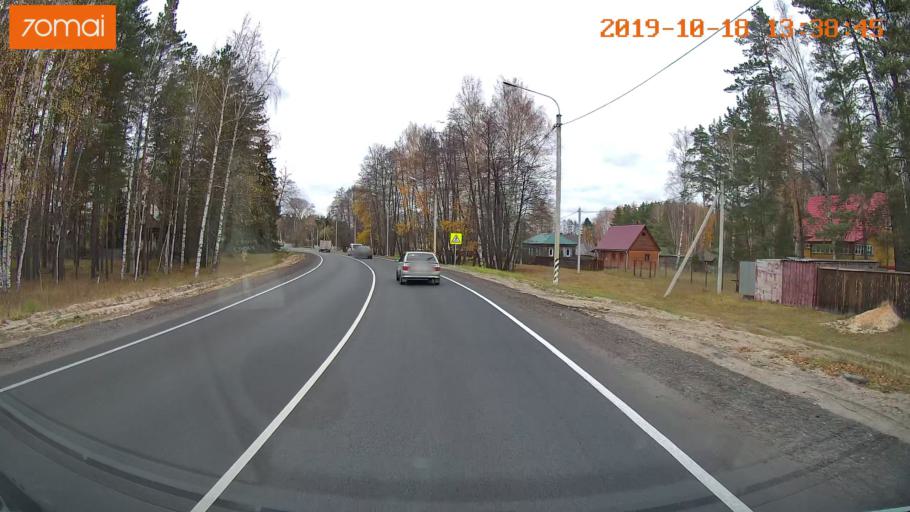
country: RU
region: Rjazan
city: Solotcha
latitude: 54.8931
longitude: 40.0027
